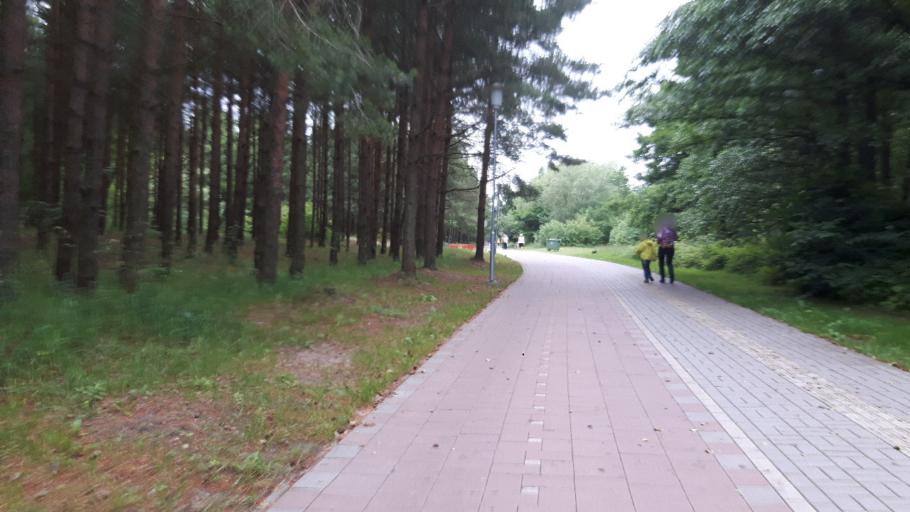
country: LV
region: Liepaja
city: Liepaja
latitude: 56.4905
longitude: 20.9983
